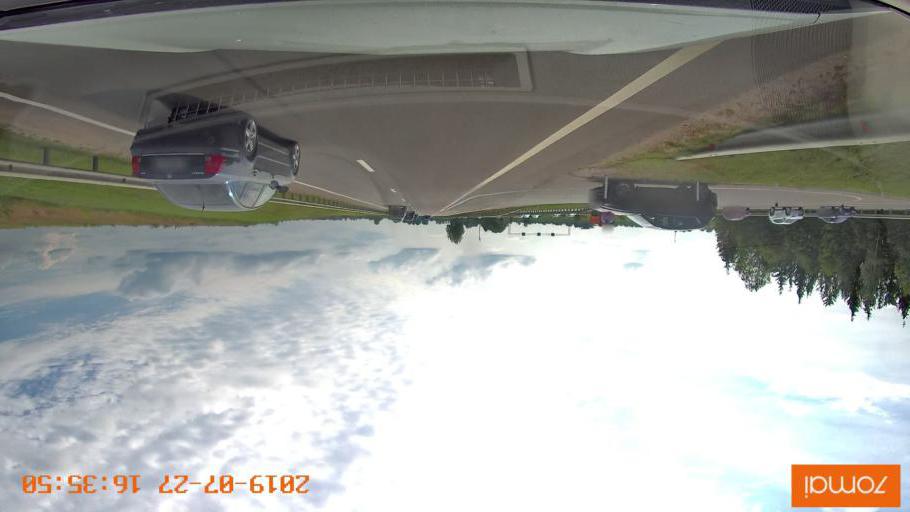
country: RU
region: Kaliningrad
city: Gvardeysk
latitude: 54.6491
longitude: 21.2998
